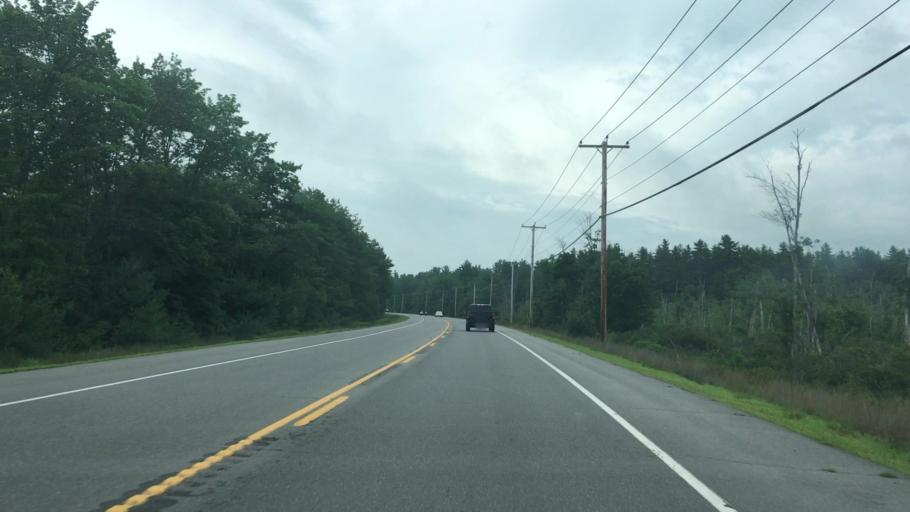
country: US
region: Maine
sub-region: York County
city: Lebanon
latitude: 43.3988
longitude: -70.8763
